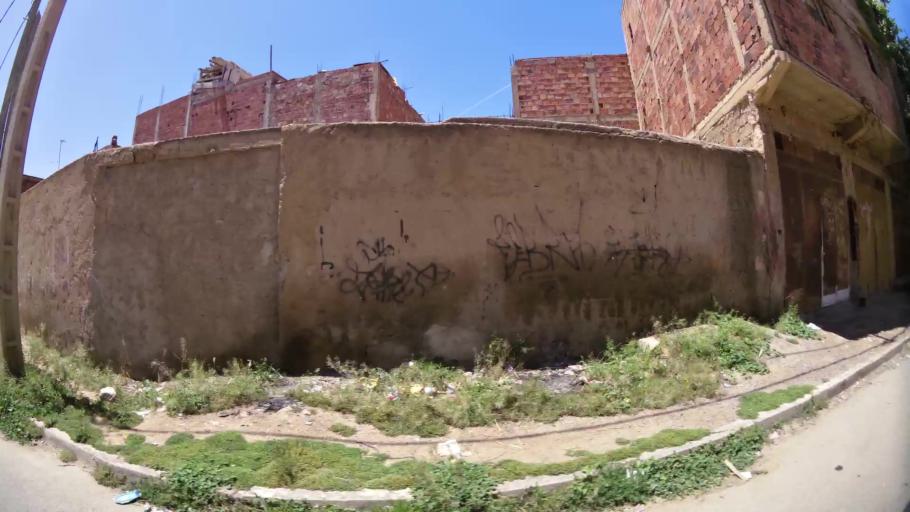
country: MA
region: Oriental
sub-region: Oujda-Angad
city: Oujda
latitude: 34.6631
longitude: -1.9248
